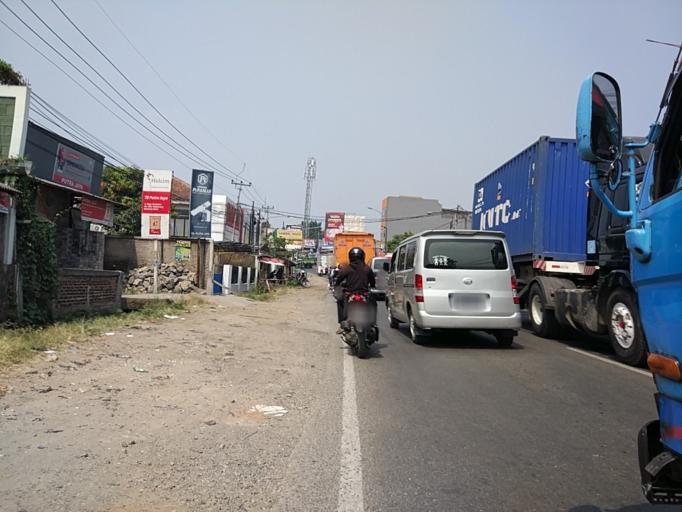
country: ID
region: West Java
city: Padalarang
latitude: -6.8581
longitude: 107.4988
